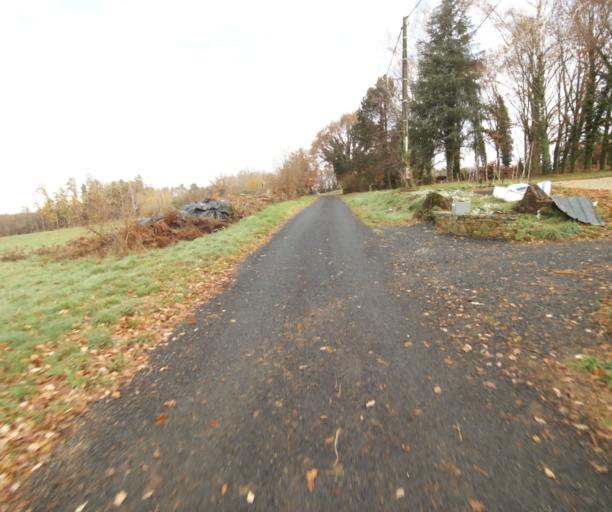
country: FR
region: Limousin
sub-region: Departement de la Correze
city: Saint-Mexant
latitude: 45.2518
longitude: 1.6464
